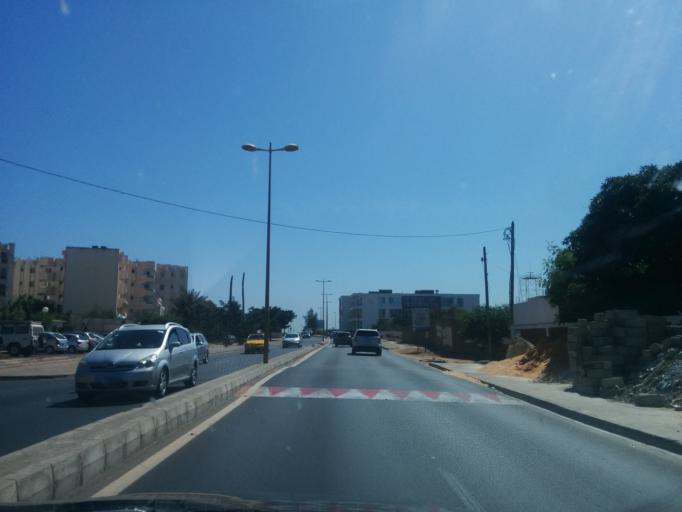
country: SN
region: Dakar
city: Mermoz Boabab
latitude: 14.7065
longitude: -17.4836
